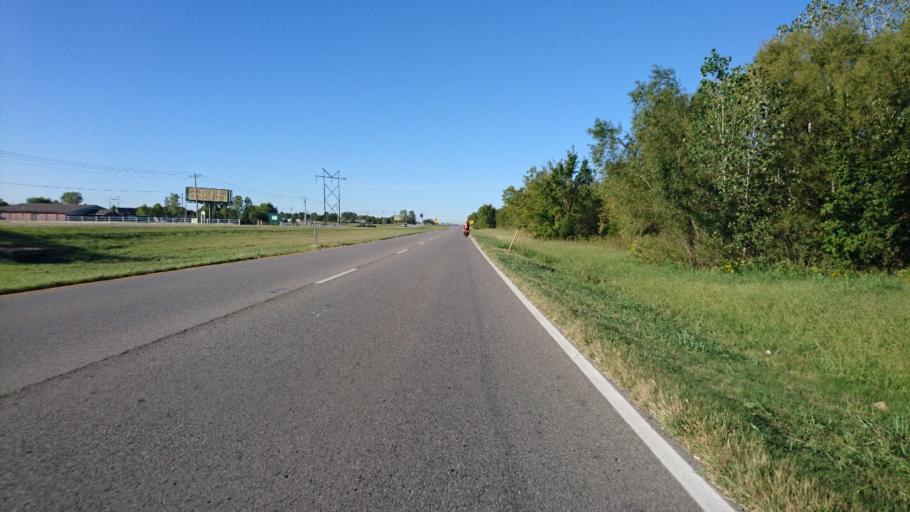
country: US
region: Oklahoma
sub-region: Rogers County
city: Verdigris
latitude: 36.2560
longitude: -95.6619
